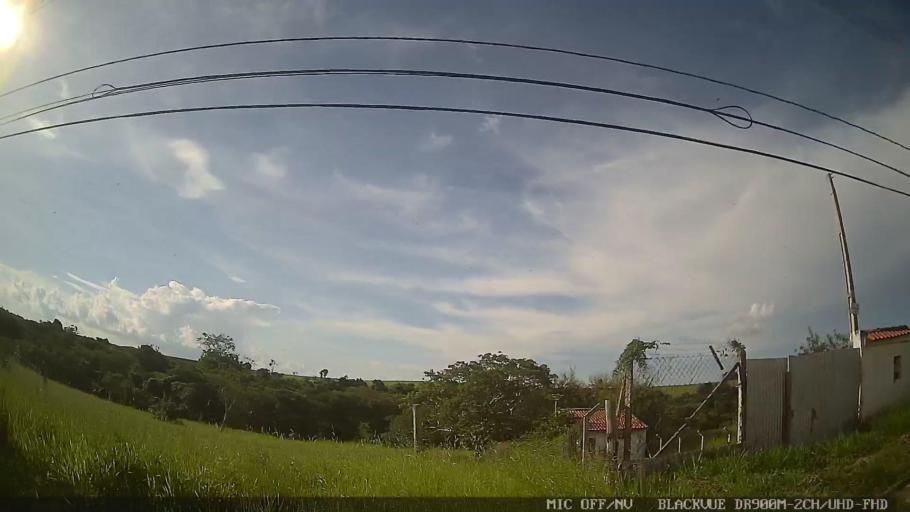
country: BR
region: Sao Paulo
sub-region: Tiete
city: Tiete
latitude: -23.0846
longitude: -47.6885
